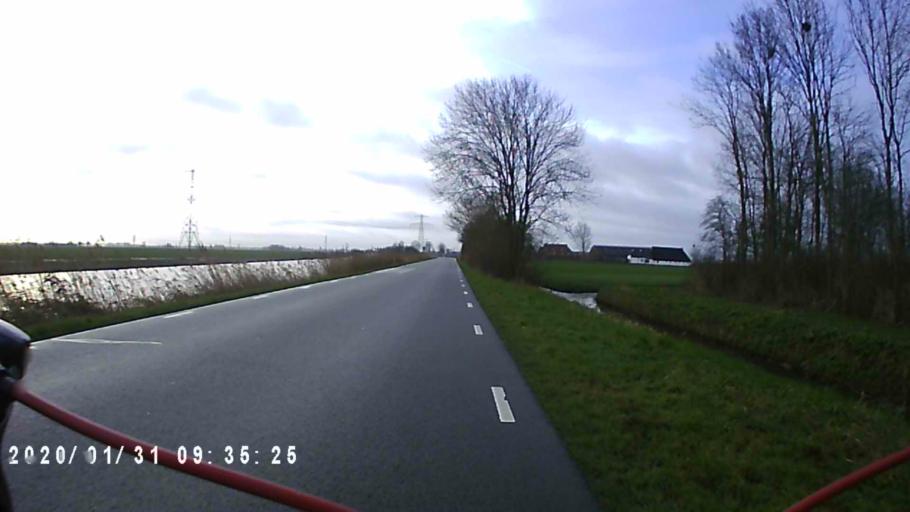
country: NL
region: Groningen
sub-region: Gemeente Winsum
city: Winsum
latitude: 53.3021
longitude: 6.4813
